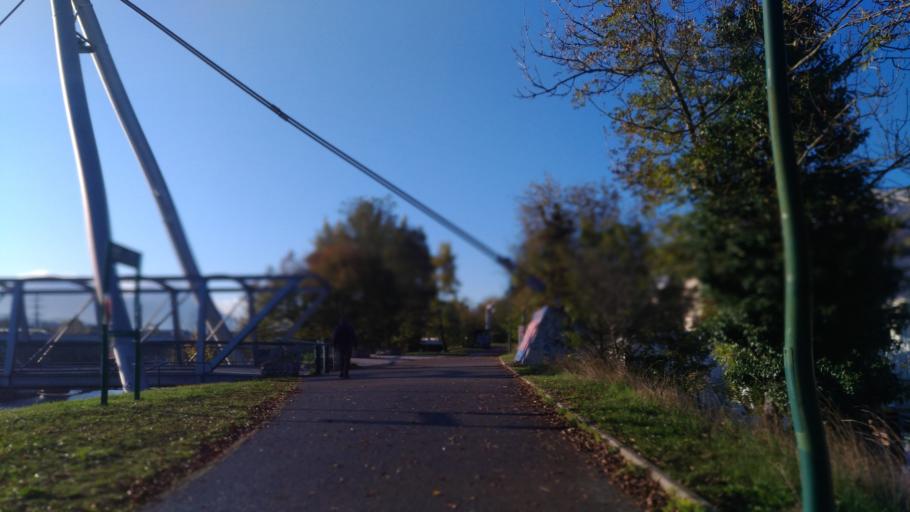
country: FR
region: Rhone-Alpes
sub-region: Departement de l'Isere
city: Seyssinet-Pariset
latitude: 45.1604
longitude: 5.6990
